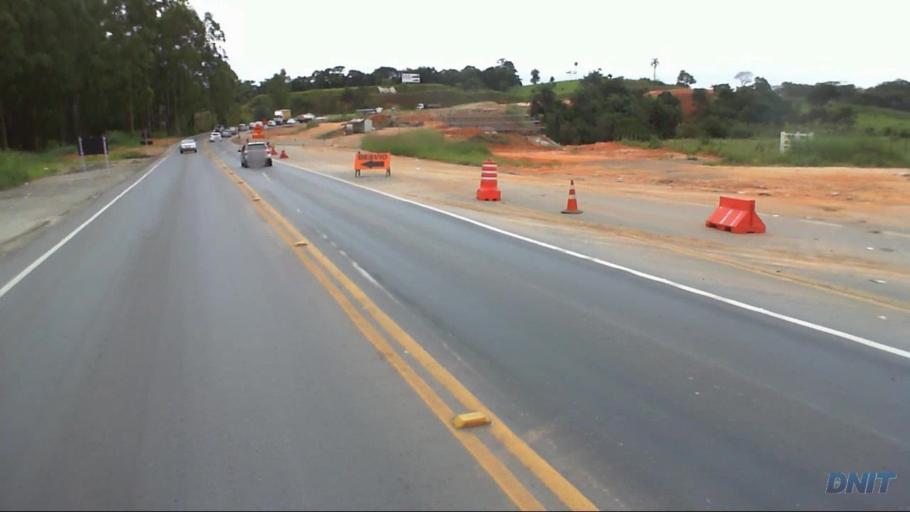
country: BR
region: Minas Gerais
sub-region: Barao De Cocais
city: Barao de Cocais
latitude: -19.7522
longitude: -43.4776
